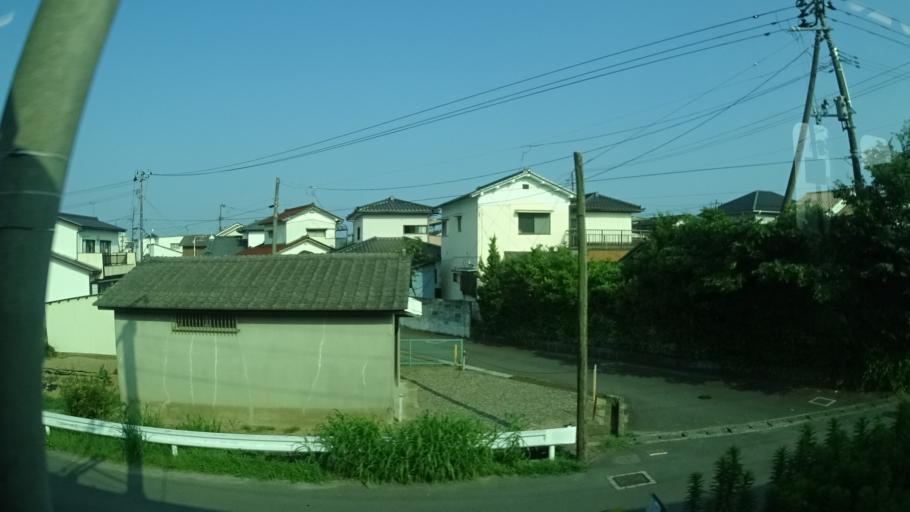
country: JP
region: Ibaraki
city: Kitaibaraki
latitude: 36.9028
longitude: 140.7839
